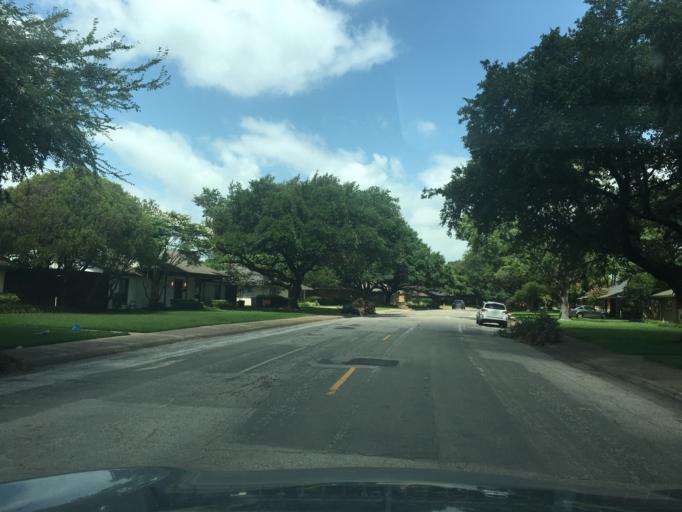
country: US
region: Texas
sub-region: Dallas County
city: Addison
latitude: 32.9212
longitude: -96.8216
